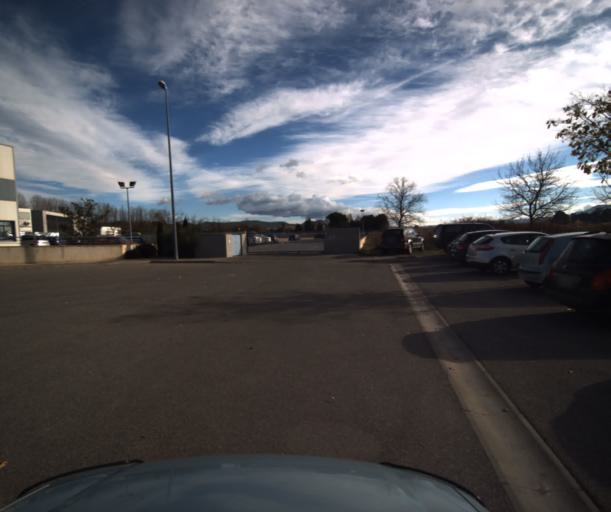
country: FR
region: Provence-Alpes-Cote d'Azur
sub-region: Departement du Vaucluse
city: Pertuis
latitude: 43.6780
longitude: 5.5047
